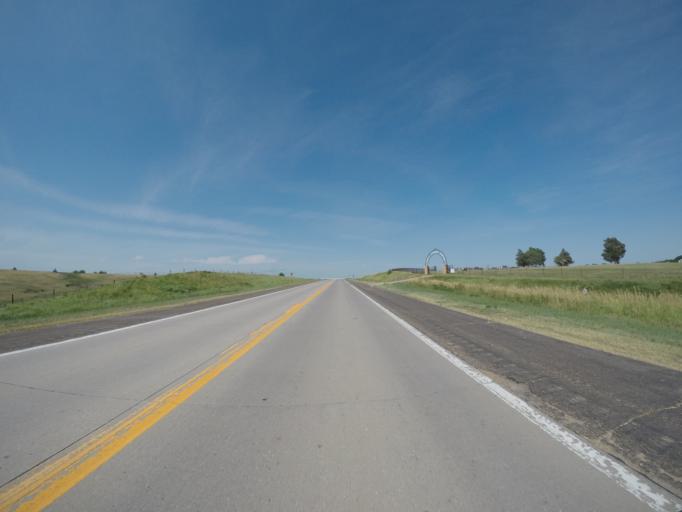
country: US
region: Nebraska
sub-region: Adams County
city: Hastings
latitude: 40.3512
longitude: -98.4419
